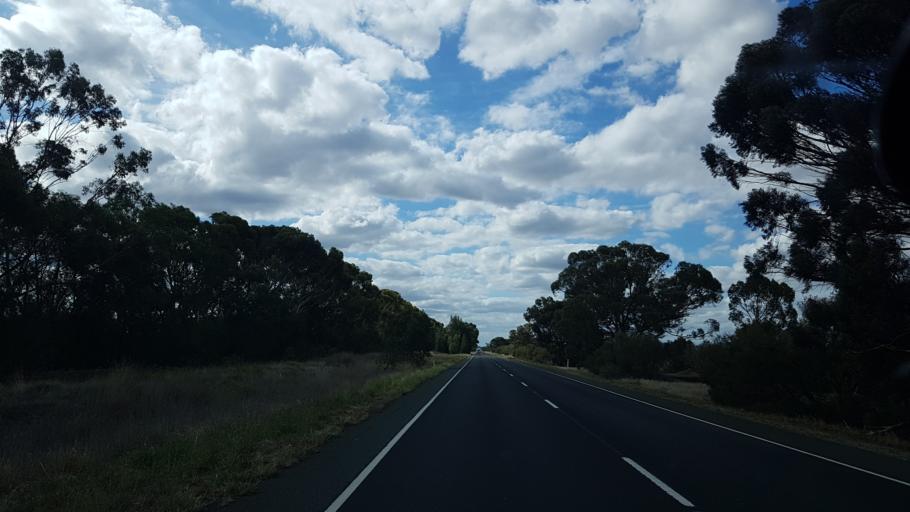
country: AU
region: Victoria
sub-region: Swan Hill
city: Swan Hill
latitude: -35.9807
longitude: 143.9449
